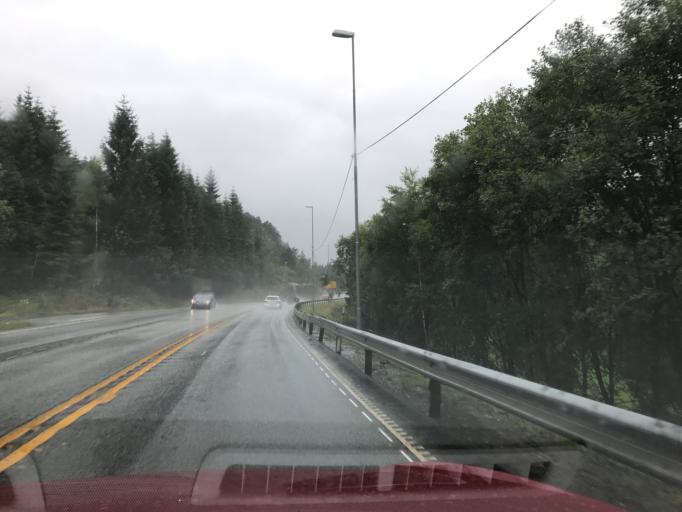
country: NO
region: Rogaland
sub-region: Lund
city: Moi
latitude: 58.3988
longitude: 6.6292
